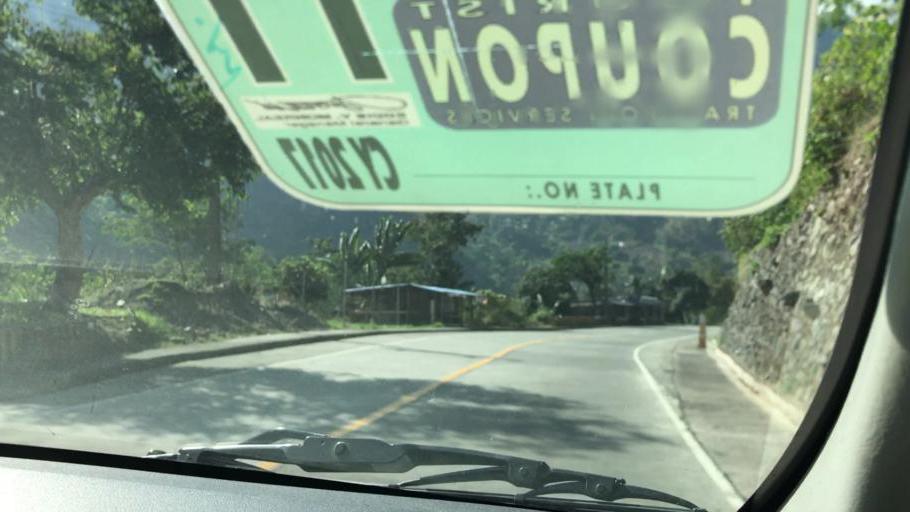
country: PH
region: Cordillera
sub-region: Province of Benguet
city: Tuba
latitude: 16.3173
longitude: 120.6179
